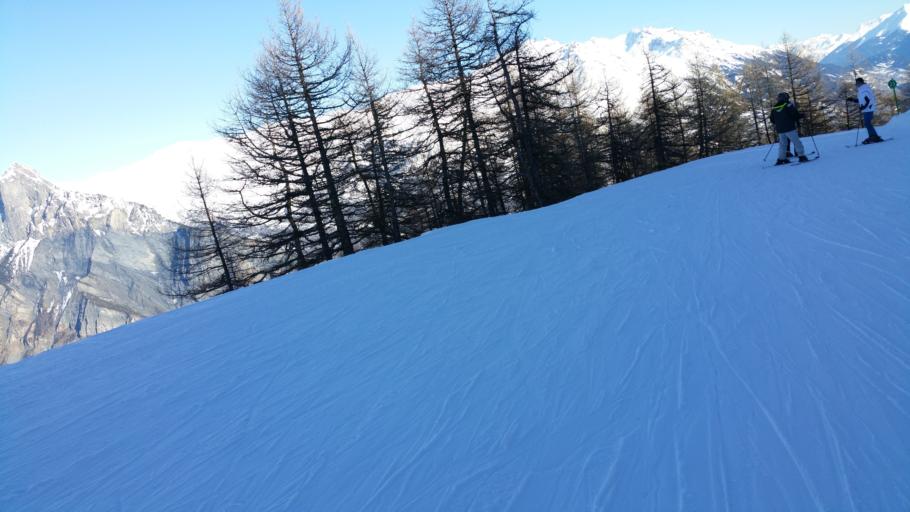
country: FR
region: Rhone-Alpes
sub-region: Departement de la Savoie
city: Villargondran
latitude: 45.2194
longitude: 6.3952
